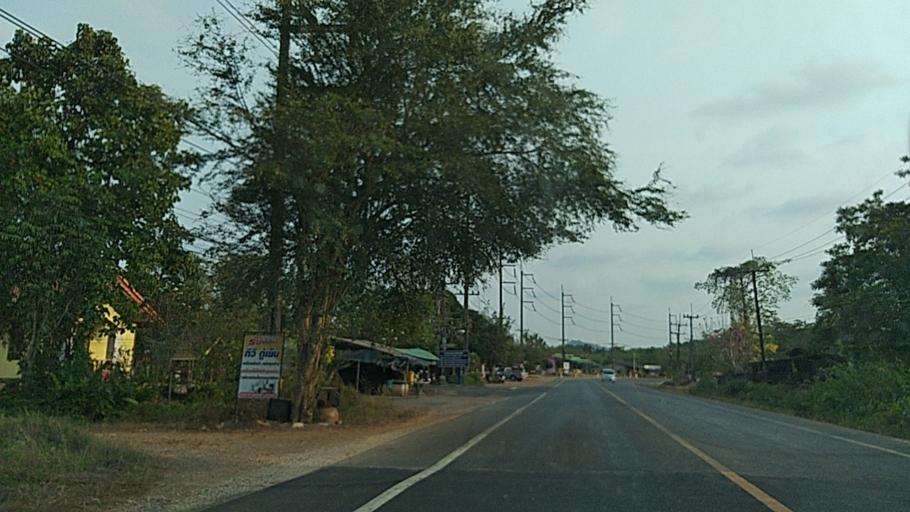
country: TH
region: Trat
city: Khao Saming
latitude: 12.3317
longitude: 102.3704
